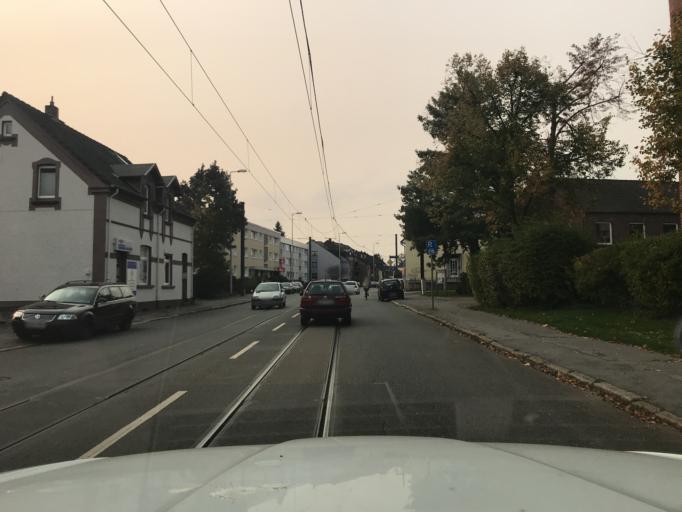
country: DE
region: North Rhine-Westphalia
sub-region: Regierungsbezirk Dusseldorf
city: Muelheim (Ruhr)
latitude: 51.4168
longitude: 6.9048
